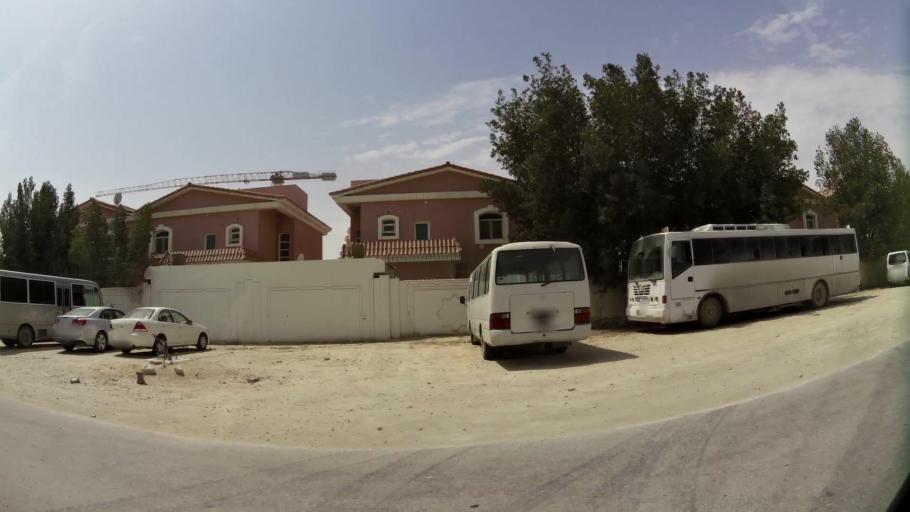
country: QA
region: Baladiyat ar Rayyan
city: Ar Rayyan
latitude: 25.3511
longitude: 51.4701
